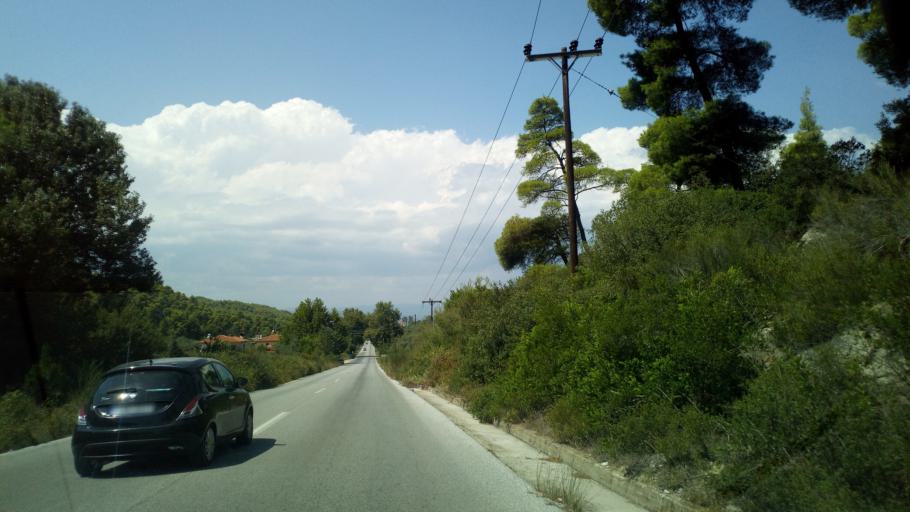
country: GR
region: Central Macedonia
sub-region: Nomos Chalkidikis
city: Agios Nikolaos
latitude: 40.2153
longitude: 23.7538
